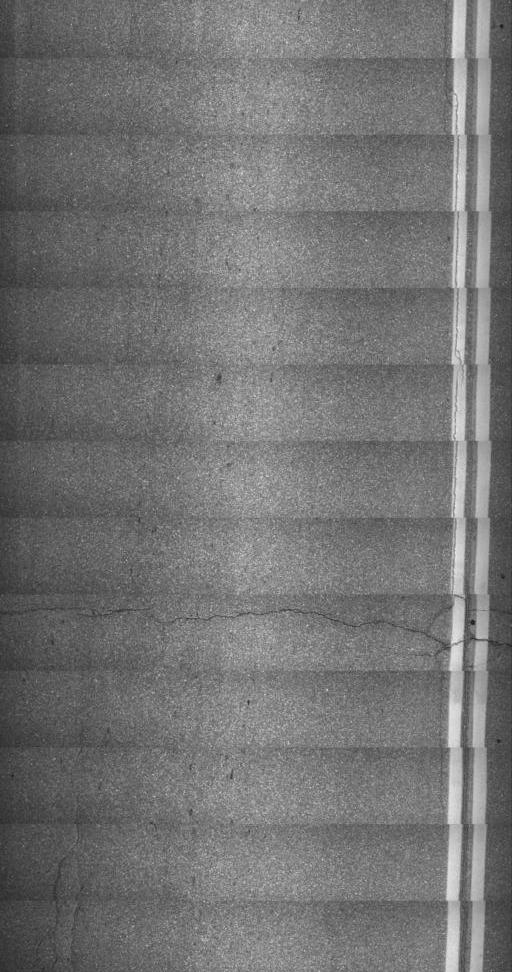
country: US
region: Vermont
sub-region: Bennington County
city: Manchester Center
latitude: 43.1789
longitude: -73.0483
